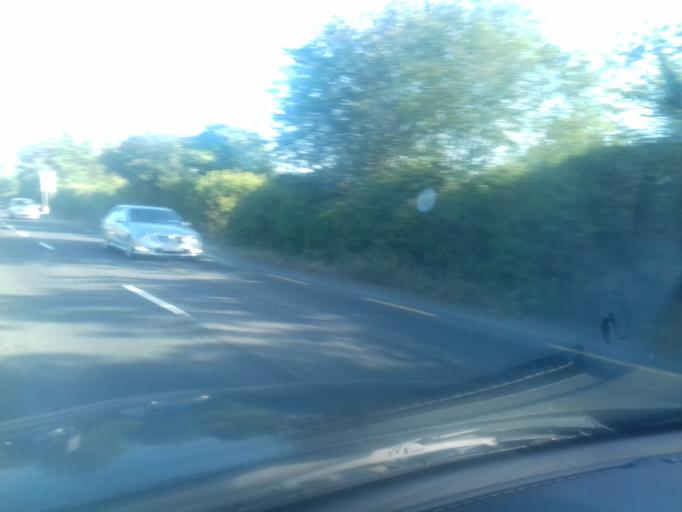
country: IE
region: Leinster
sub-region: An Mhi
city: Ashbourne
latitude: 53.4650
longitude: -6.3560
